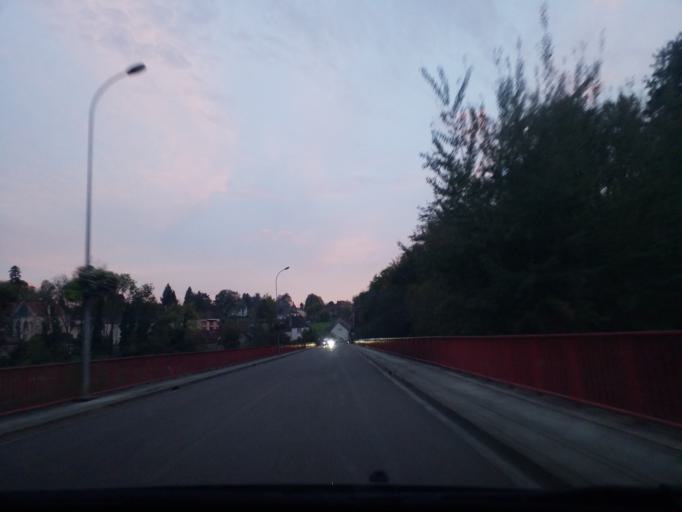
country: FR
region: Franche-Comte
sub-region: Departement de la Haute-Saone
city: Villersexel
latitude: 47.5547
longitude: 6.4350
